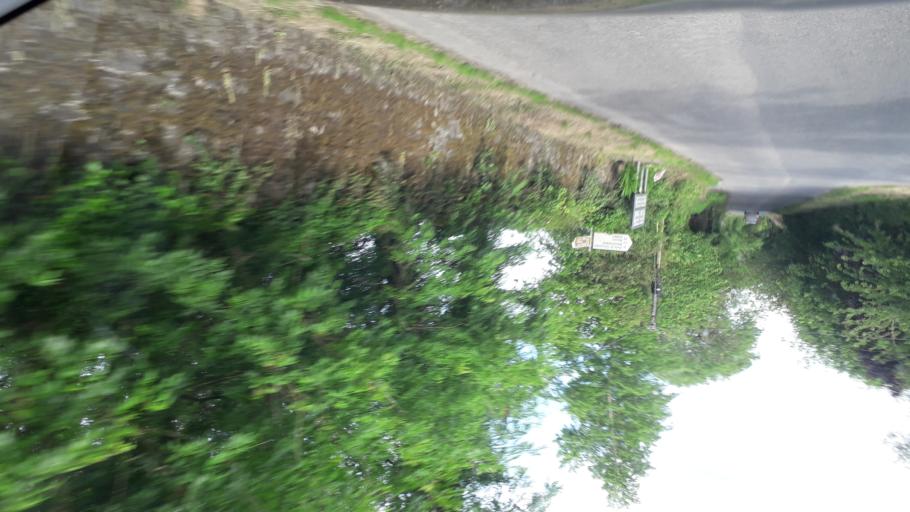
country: IE
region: Leinster
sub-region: Loch Garman
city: Ballinroad
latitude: 52.5190
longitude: -6.2765
